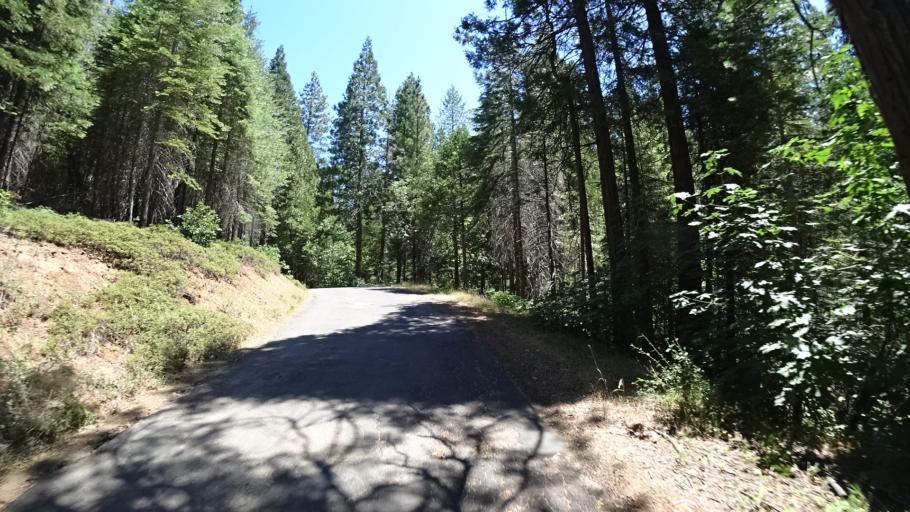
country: US
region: California
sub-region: Calaveras County
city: Arnold
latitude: 38.2200
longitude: -120.3371
